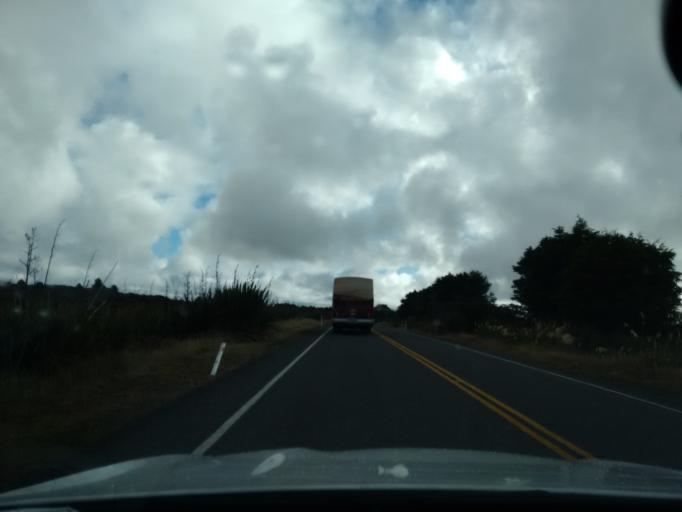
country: NZ
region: Manawatu-Wanganui
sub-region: Ruapehu District
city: Waiouru
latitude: -39.1790
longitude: 175.4596
